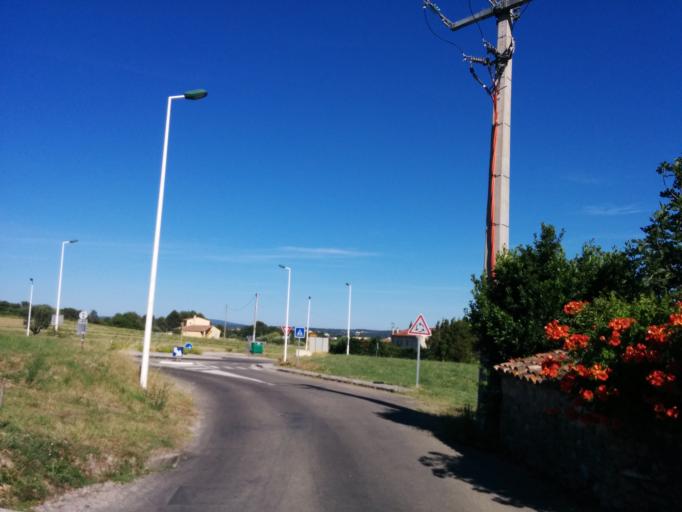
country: FR
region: Languedoc-Roussillon
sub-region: Departement du Gard
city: Saint-Christol-les-Ales
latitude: 44.0920
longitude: 4.0640
